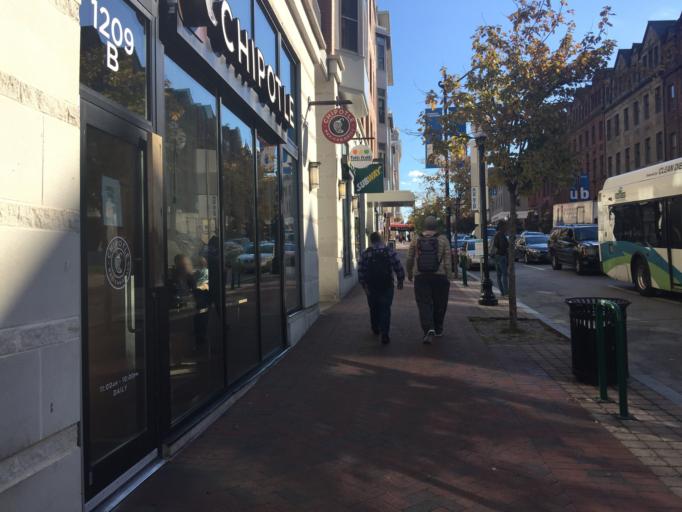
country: US
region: Maryland
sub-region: City of Baltimore
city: Baltimore
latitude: 39.3044
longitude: -76.6160
